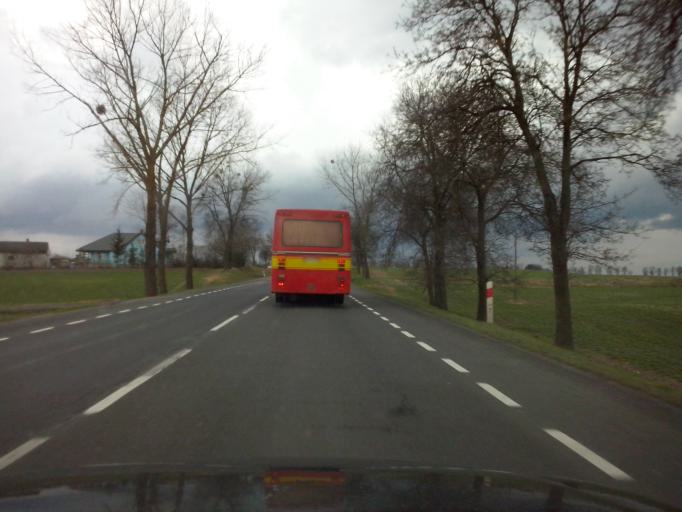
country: PL
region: Lublin Voivodeship
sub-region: Powiat chelmski
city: Rejowiec Fabryczny
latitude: 51.1734
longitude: 23.2780
